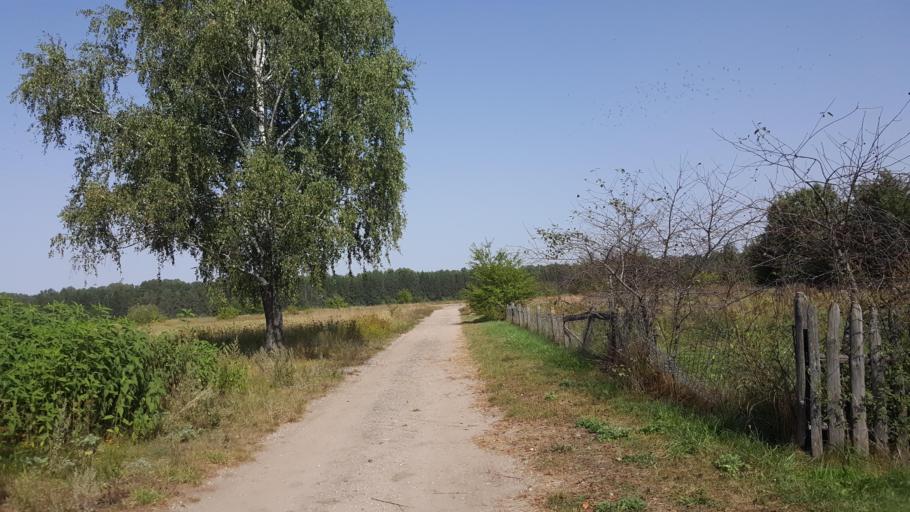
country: BY
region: Brest
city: Pruzhany
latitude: 52.4909
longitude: 24.6064
